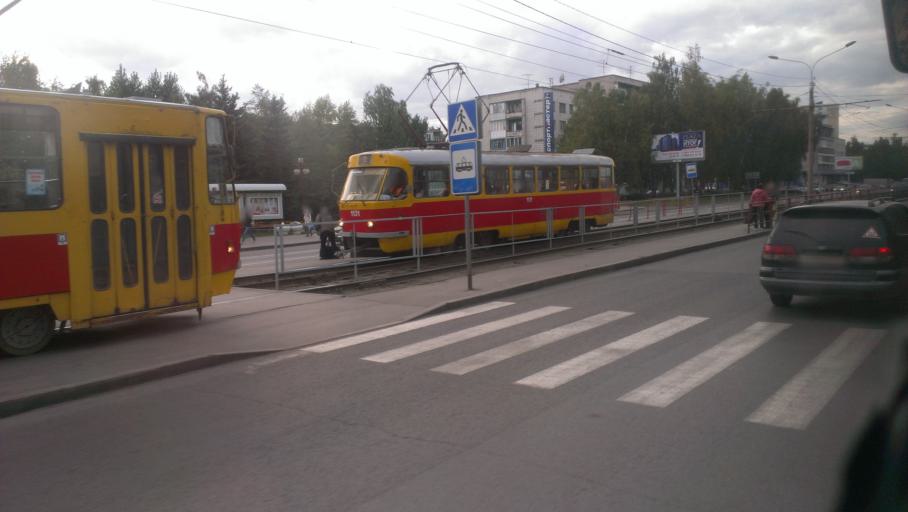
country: RU
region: Altai Krai
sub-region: Gorod Barnaulskiy
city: Barnaul
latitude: 53.3449
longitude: 83.7662
